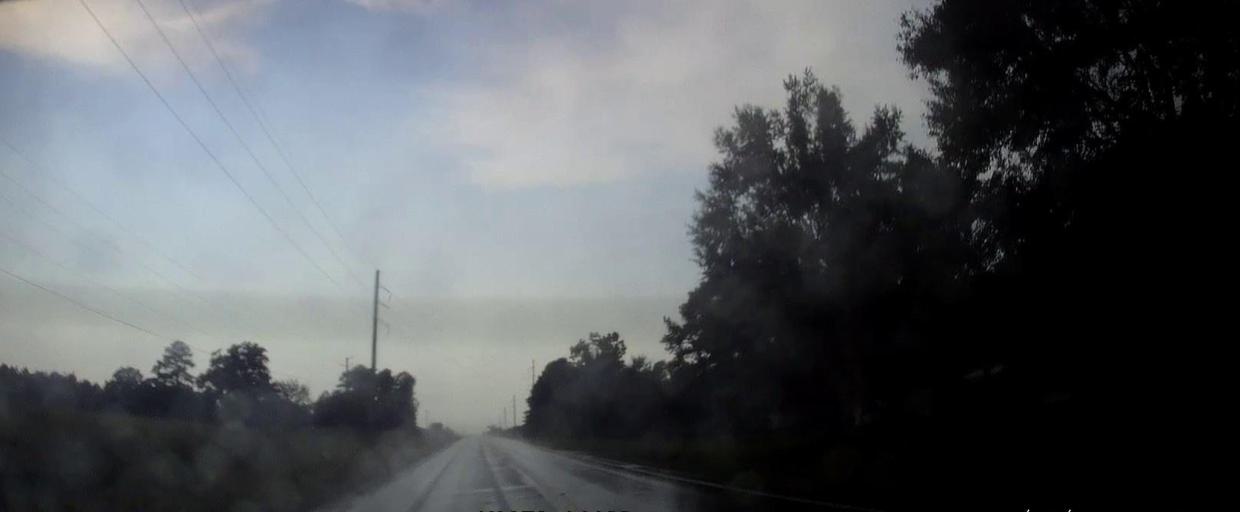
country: US
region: Georgia
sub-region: Twiggs County
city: Jeffersonville
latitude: 32.5754
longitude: -83.2025
